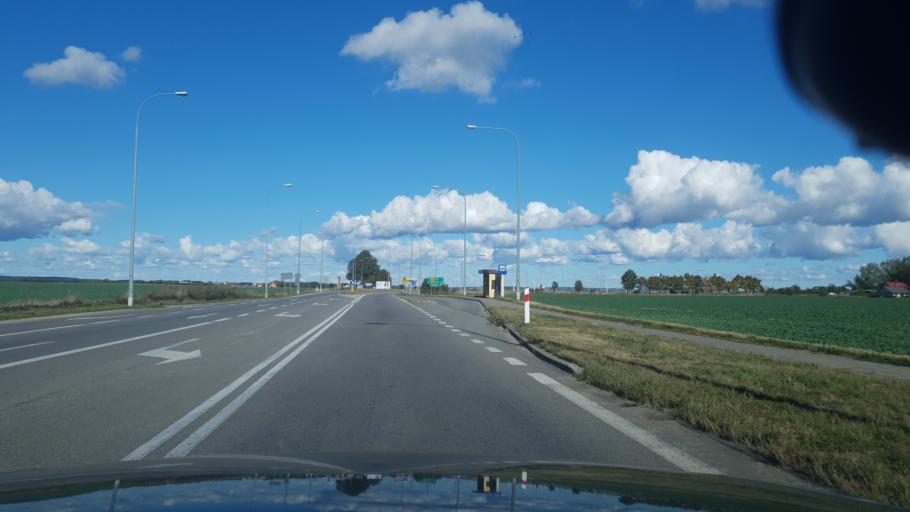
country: PL
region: Pomeranian Voivodeship
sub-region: Powiat pucki
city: Zelistrzewo
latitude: 54.6858
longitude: 18.3695
